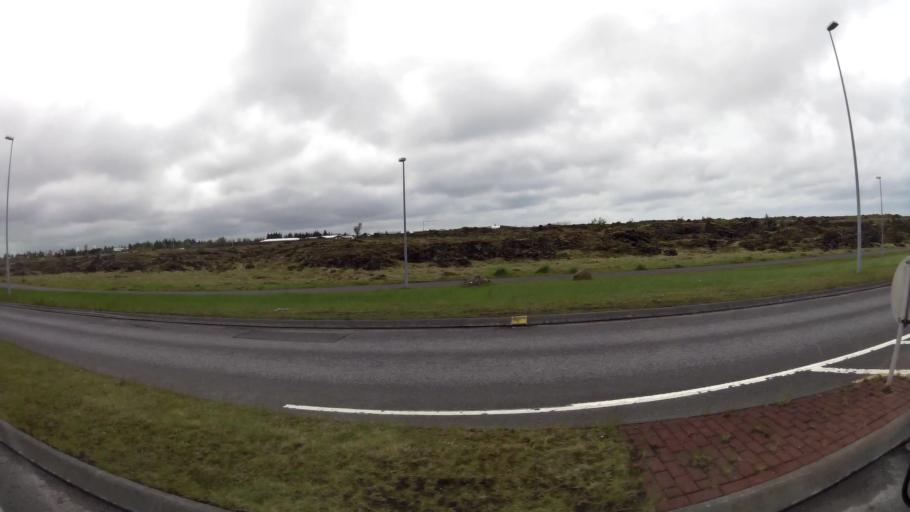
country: IS
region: Capital Region
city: Hafnarfjoerdur
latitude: 64.0887
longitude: -21.9530
